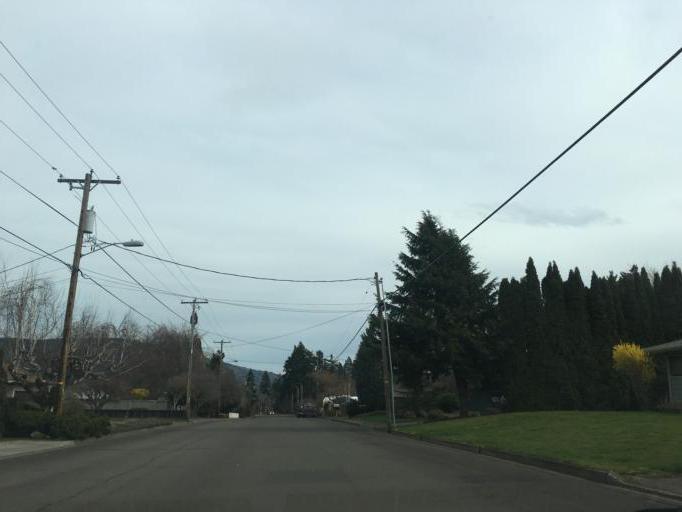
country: US
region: Oregon
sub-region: Hood River County
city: Hood River
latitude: 45.7074
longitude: -121.5319
